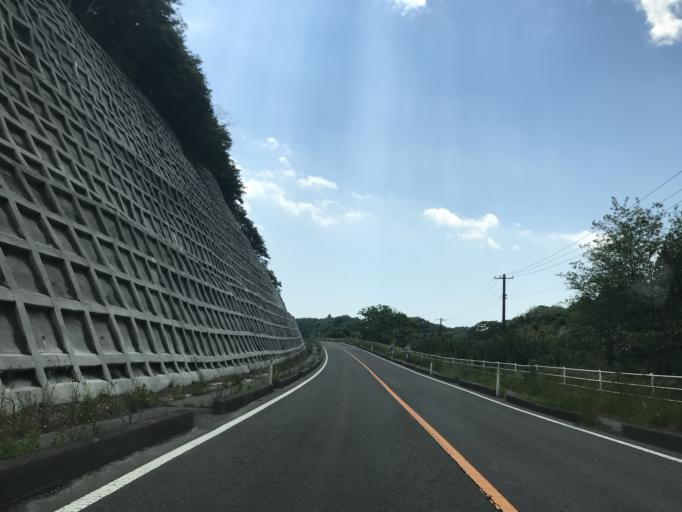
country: JP
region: Miyagi
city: Matsushima
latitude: 38.4075
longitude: 141.0658
